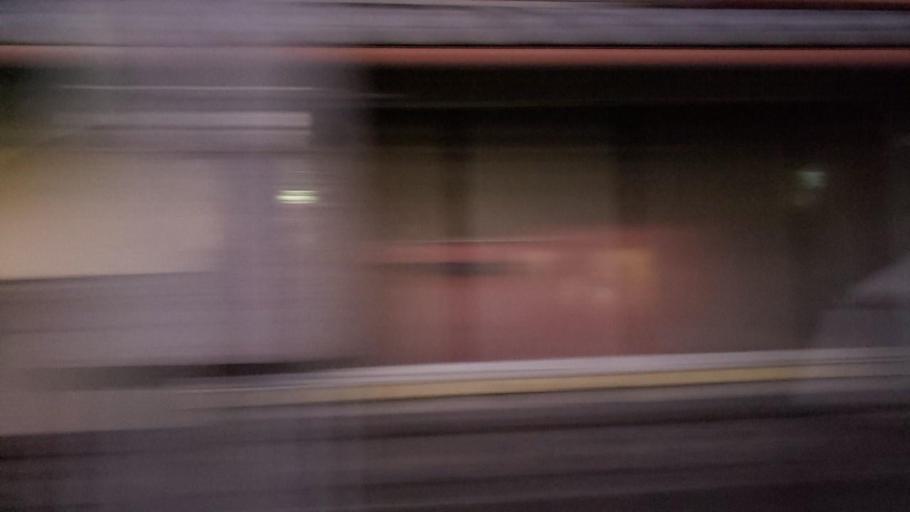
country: JP
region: Tokushima
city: Kamojimacho-jogejima
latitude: 34.0875
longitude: 134.2914
